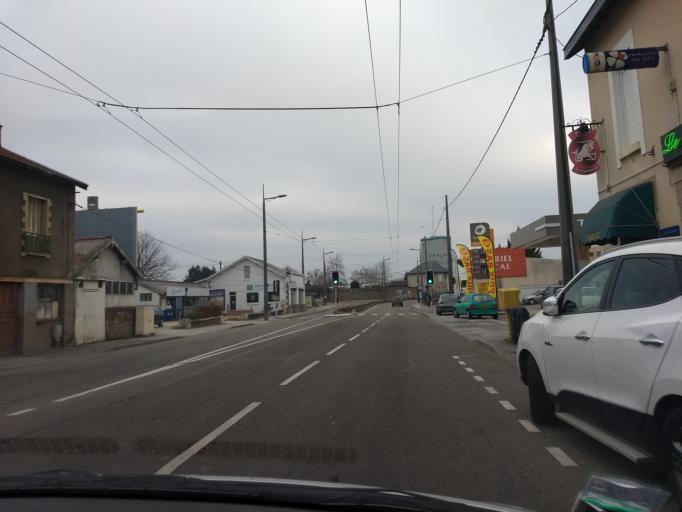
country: FR
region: Limousin
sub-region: Departement de la Haute-Vienne
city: Limoges
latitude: 45.8541
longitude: 1.2662
